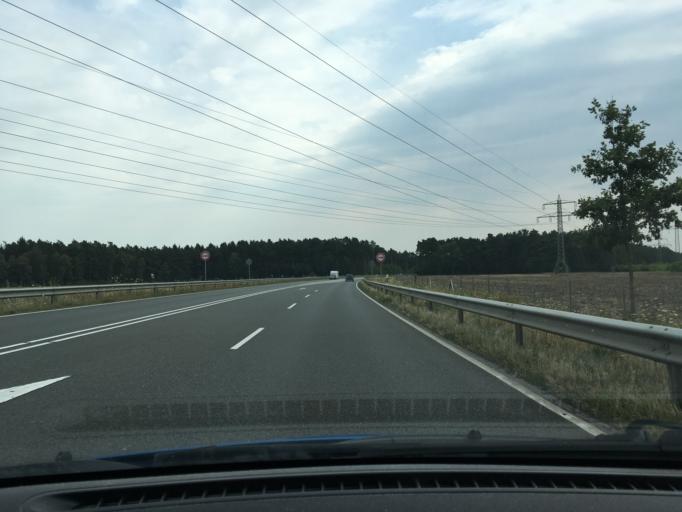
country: DE
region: Lower Saxony
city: Adelheidsdorf
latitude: 52.5741
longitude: 10.0777
